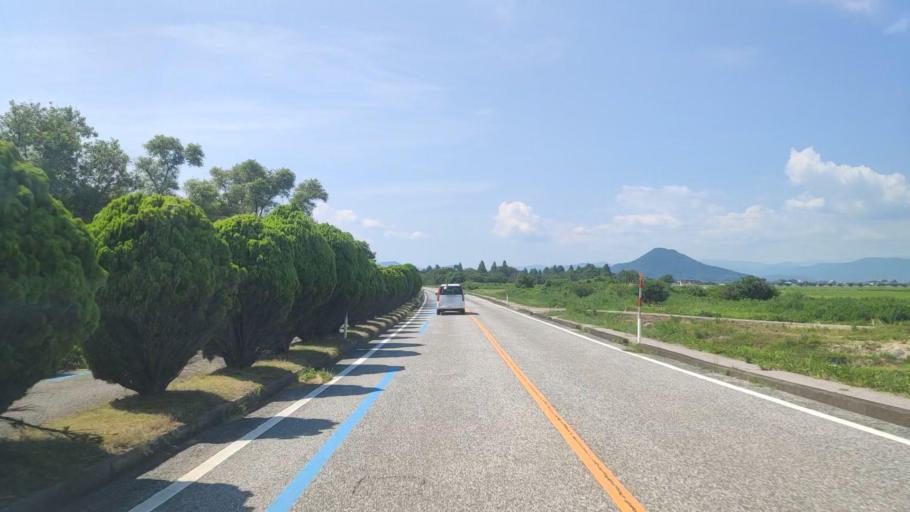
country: JP
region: Shiga Prefecture
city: Nagahama
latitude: 35.4049
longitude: 136.2143
